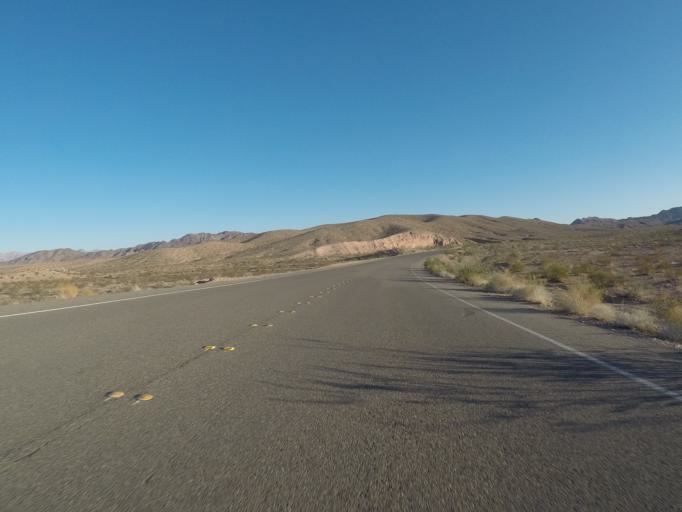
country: US
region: Nevada
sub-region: Clark County
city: Moapa Valley
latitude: 36.2923
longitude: -114.4893
